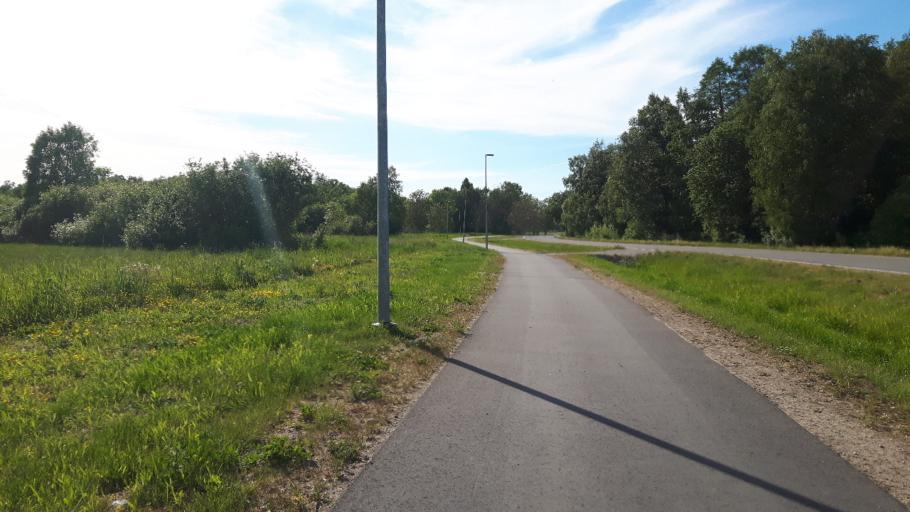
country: EE
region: Harju
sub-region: Joelaehtme vald
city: Loo
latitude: 59.4279
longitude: 24.9870
